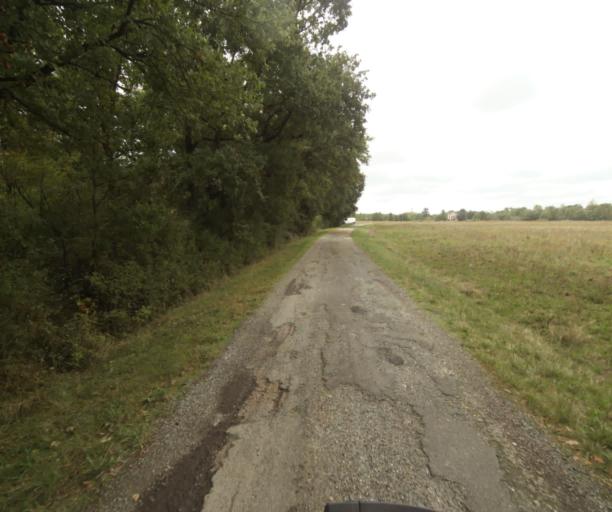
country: FR
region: Midi-Pyrenees
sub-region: Departement du Tarn-et-Garonne
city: Montech
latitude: 43.9734
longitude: 1.2525
